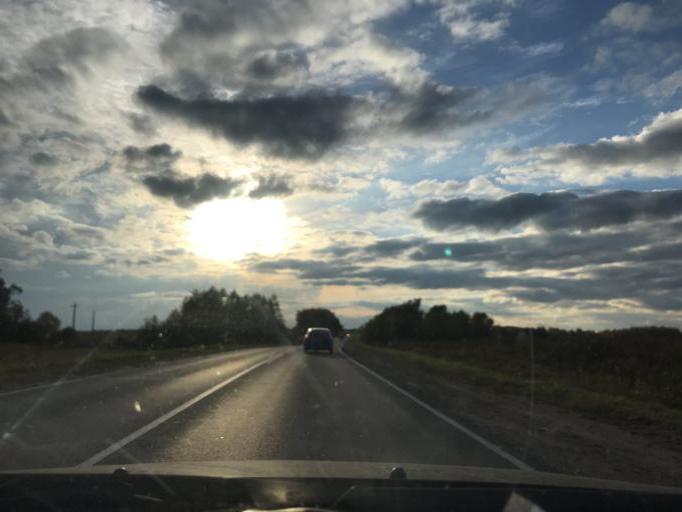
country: RU
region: Kaluga
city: Kurovskoye
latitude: 54.5230
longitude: 35.8978
